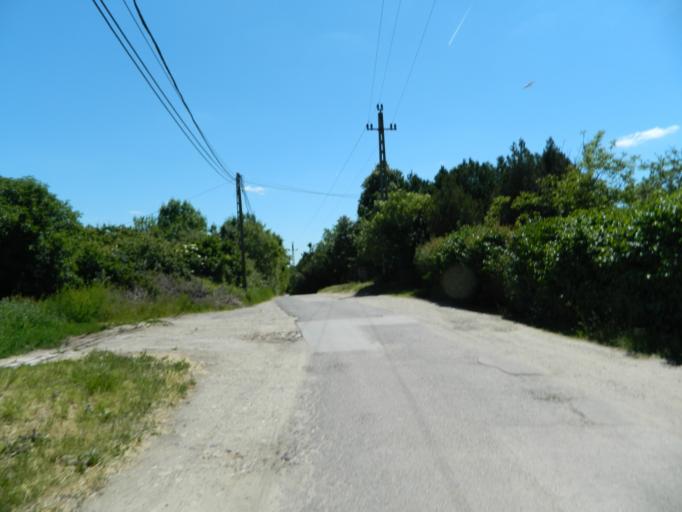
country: HU
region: Pest
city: Budakalasz
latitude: 47.6093
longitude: 19.0482
